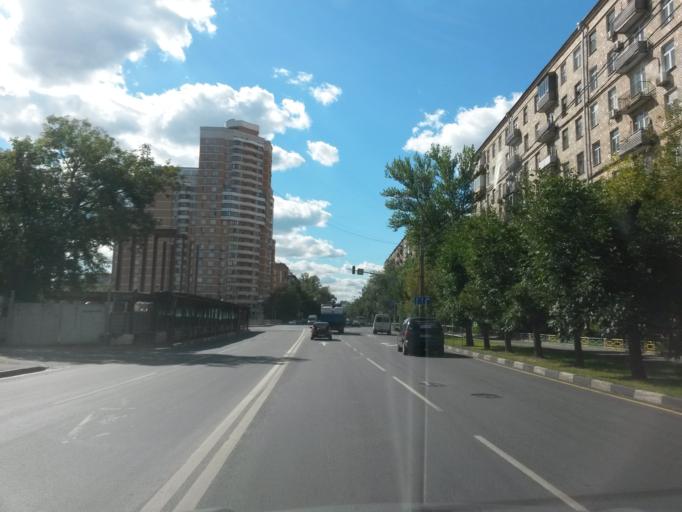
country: RU
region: Moskovskaya
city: Kozhukhovo
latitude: 55.7030
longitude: 37.6698
